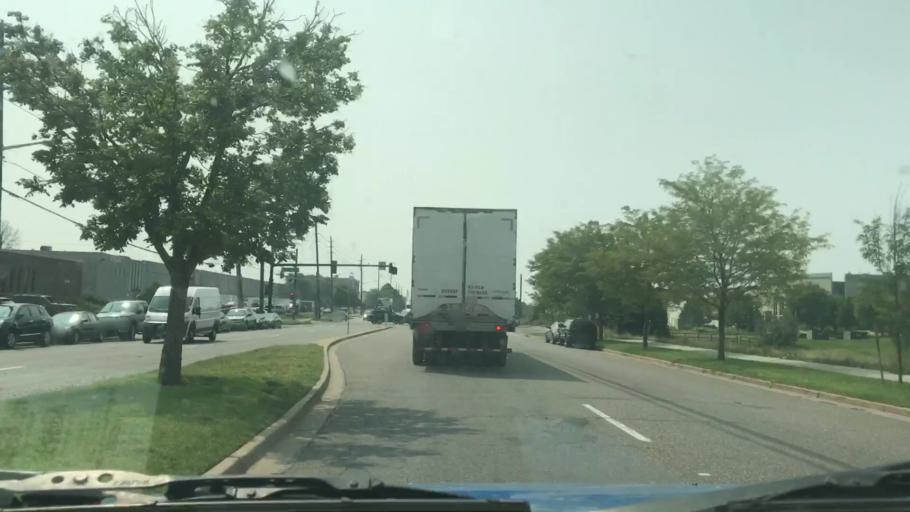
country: US
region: Colorado
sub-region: Adams County
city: Aurora
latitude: 39.7840
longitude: -104.8659
